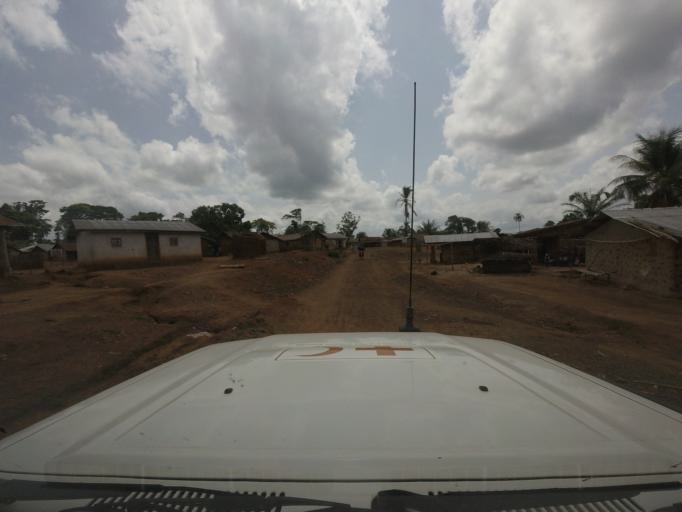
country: GN
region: Nzerekore
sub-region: Yomou
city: Yomou
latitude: 7.2870
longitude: -9.2167
